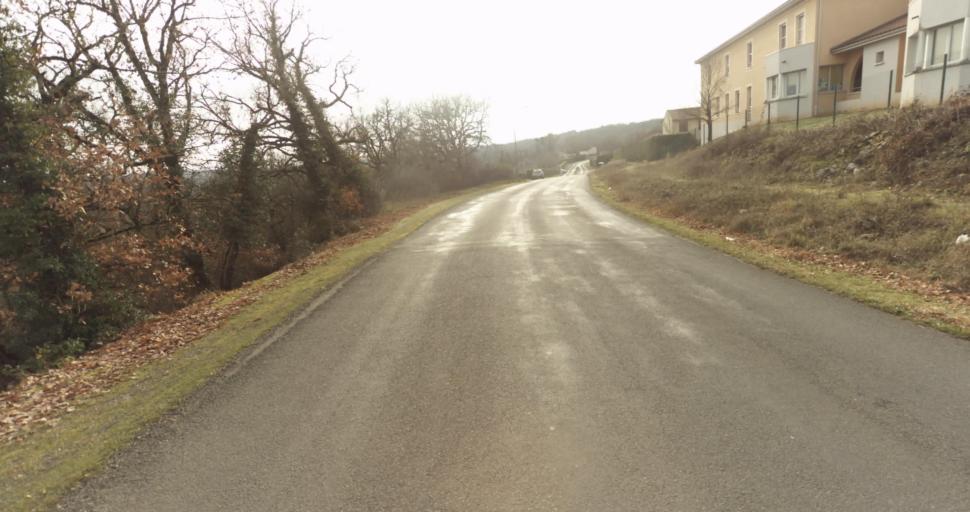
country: FR
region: Midi-Pyrenees
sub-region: Departement du Lot
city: Figeac
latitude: 44.6104
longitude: 2.0119
